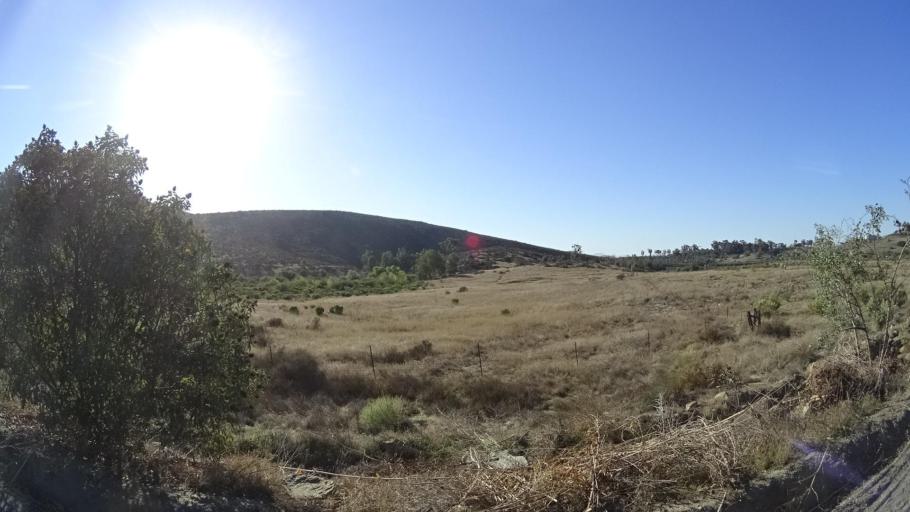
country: US
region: California
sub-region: San Diego County
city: La Presa
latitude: 32.6583
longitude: -116.9339
